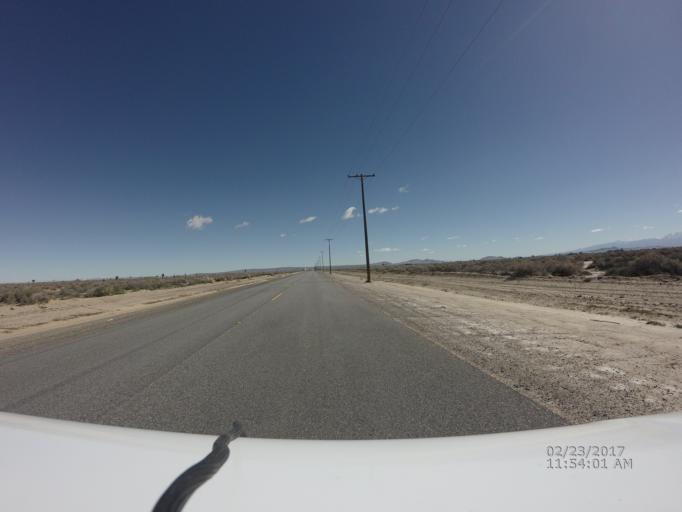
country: US
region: California
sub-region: Los Angeles County
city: Lancaster
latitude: 34.7342
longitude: -117.9860
